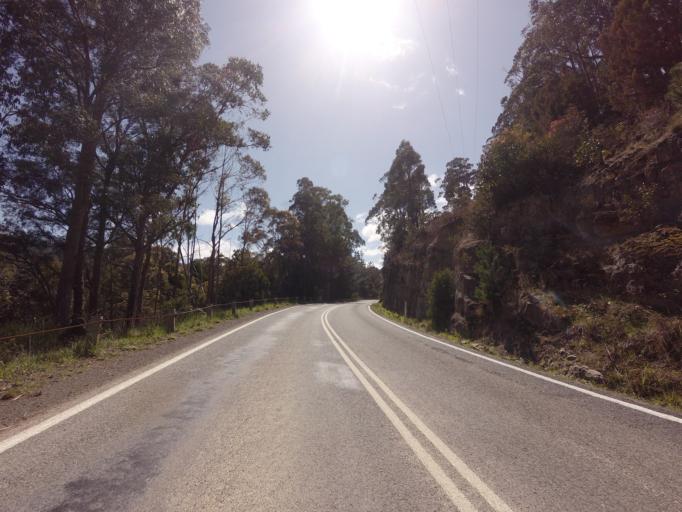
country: AU
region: Tasmania
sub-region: Derwent Valley
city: New Norfolk
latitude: -42.6924
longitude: 146.7148
